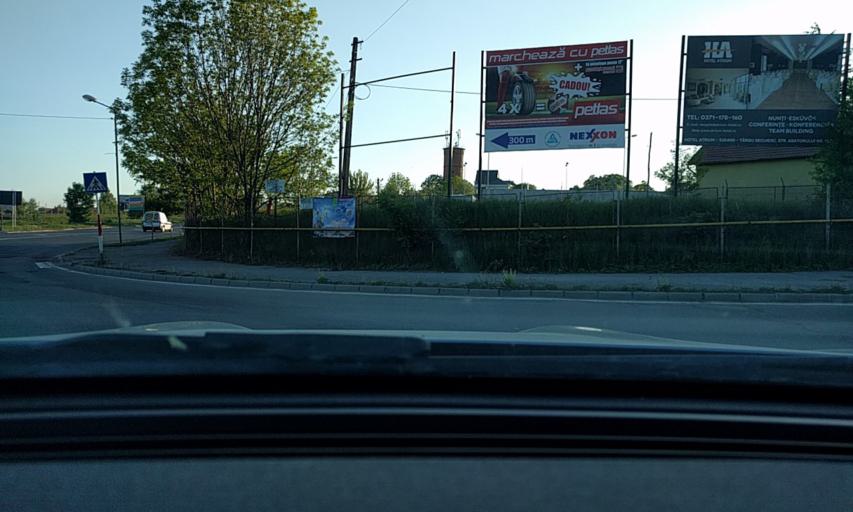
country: RO
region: Covasna
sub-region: Municipiul Targu Secuiesc
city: Targu Secuiesc
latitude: 45.9986
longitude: 26.1437
